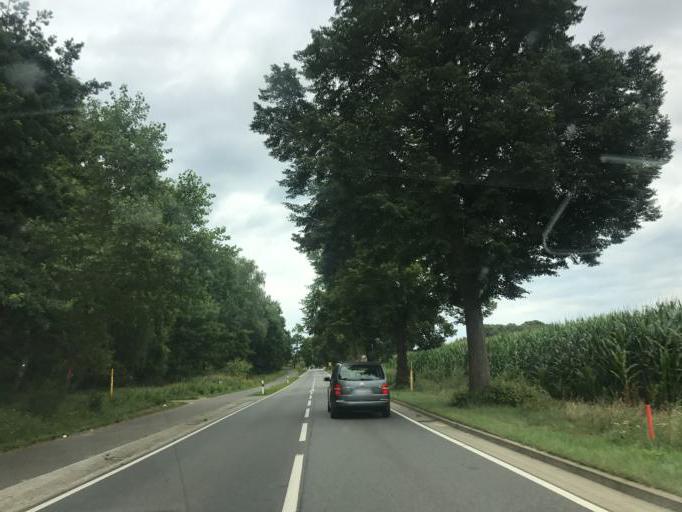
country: DE
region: Mecklenburg-Vorpommern
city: Rechlin
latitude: 53.2684
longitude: 12.7953
